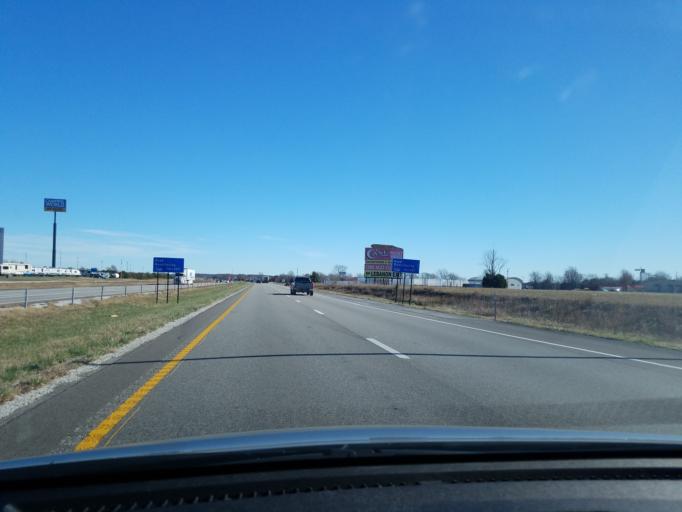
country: US
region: Missouri
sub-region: Greene County
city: Strafford
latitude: 37.2718
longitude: -93.1084
